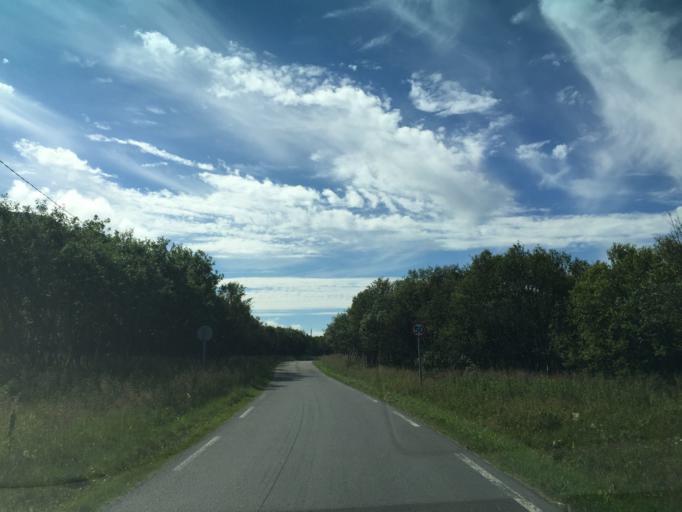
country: NO
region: Nordland
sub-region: Vagan
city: Svolvaer
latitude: 68.3993
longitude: 14.4978
